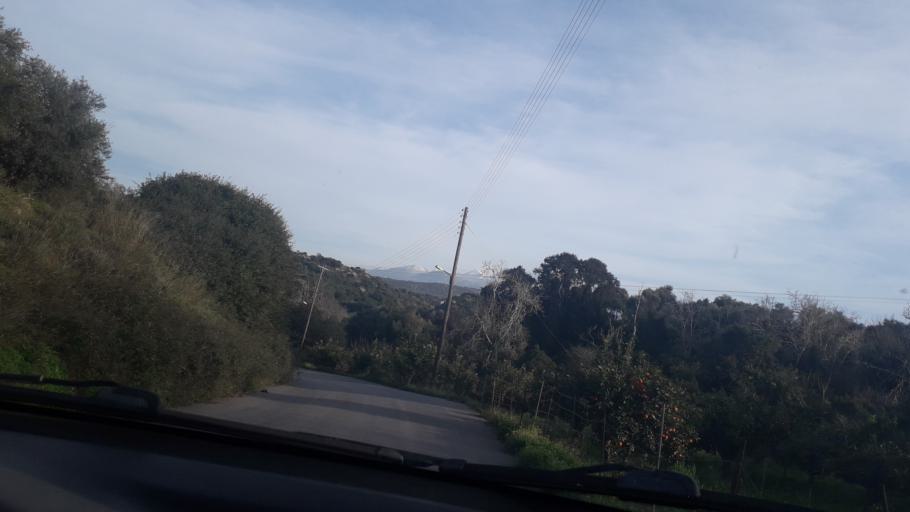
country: GR
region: Crete
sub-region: Nomos Rethymnis
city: Panormos
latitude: 35.3815
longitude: 24.6209
